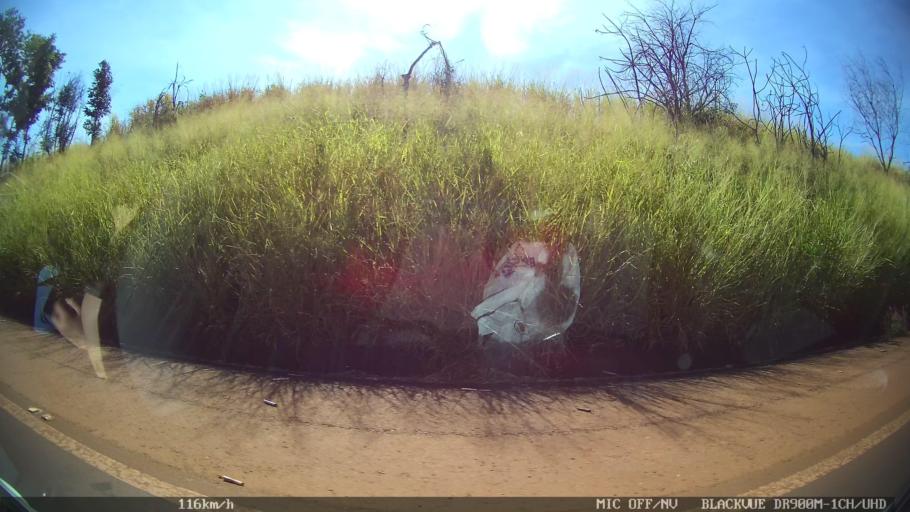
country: BR
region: Sao Paulo
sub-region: Sao Joaquim Da Barra
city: Sao Joaquim da Barra
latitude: -20.5502
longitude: -47.7470
